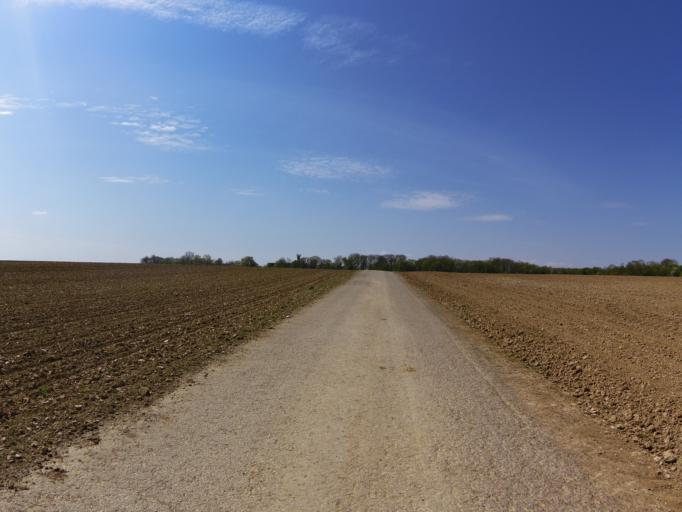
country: DE
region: Bavaria
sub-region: Regierungsbezirk Unterfranken
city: Giebelstadt
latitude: 49.6930
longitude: 9.9575
